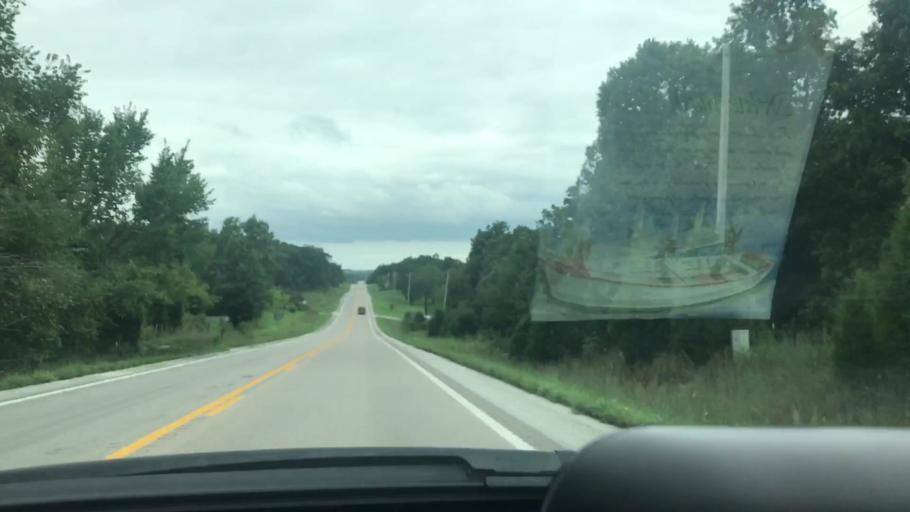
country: US
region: Missouri
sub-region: Dallas County
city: Buffalo
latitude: 37.7078
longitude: -93.1126
